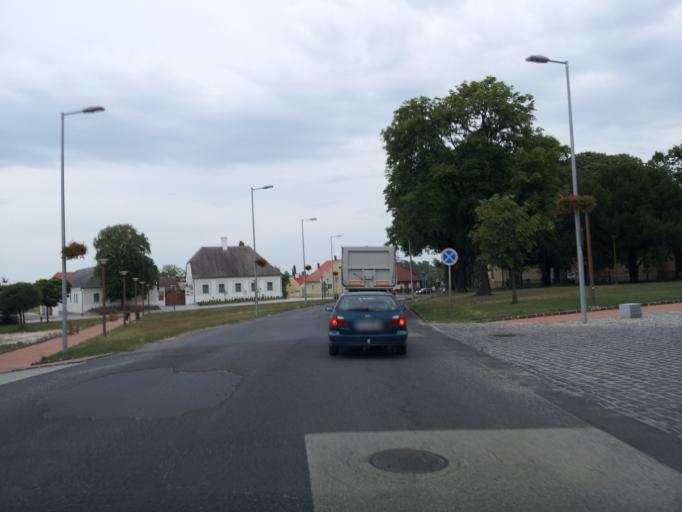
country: HU
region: Veszprem
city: Devecser
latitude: 47.1055
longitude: 17.4370
